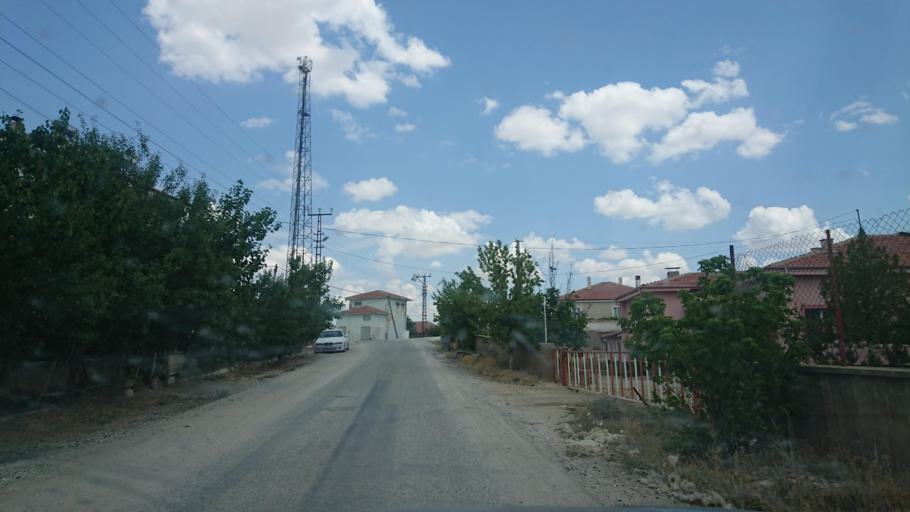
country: TR
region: Aksaray
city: Agacoren
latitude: 38.8753
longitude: 33.9122
